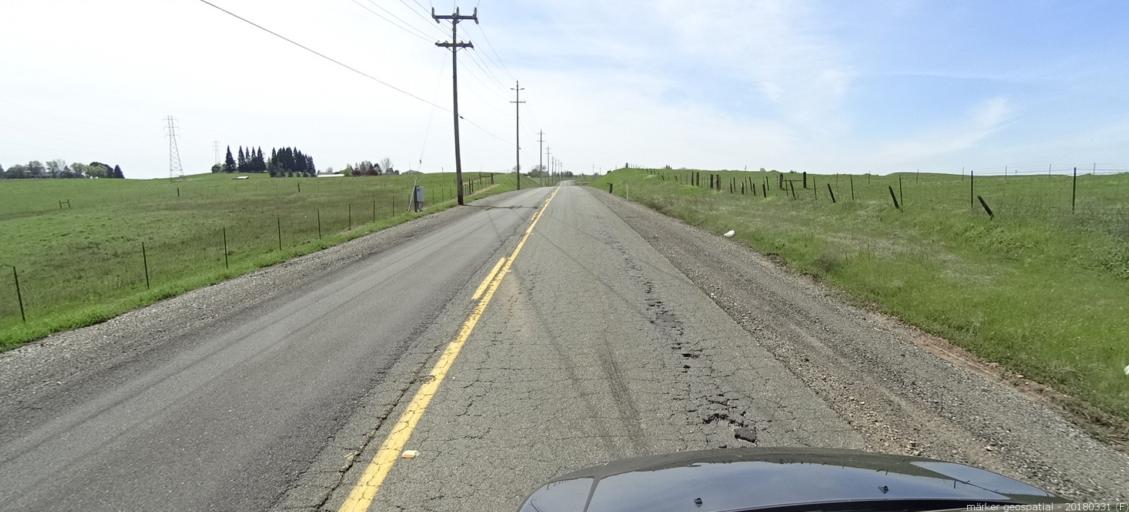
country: US
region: California
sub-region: Sacramento County
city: Rancho Murieta
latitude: 38.5021
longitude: -121.1424
